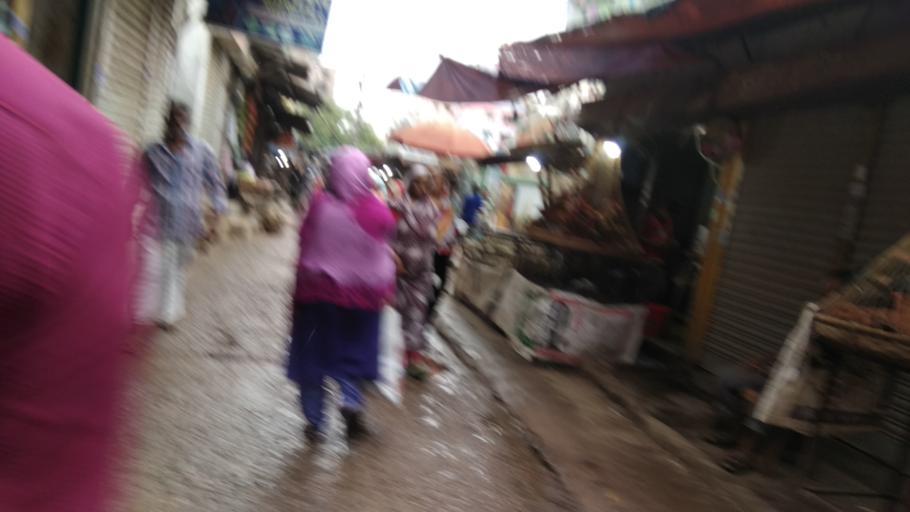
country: BD
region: Dhaka
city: Tungi
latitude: 23.8266
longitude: 90.3698
